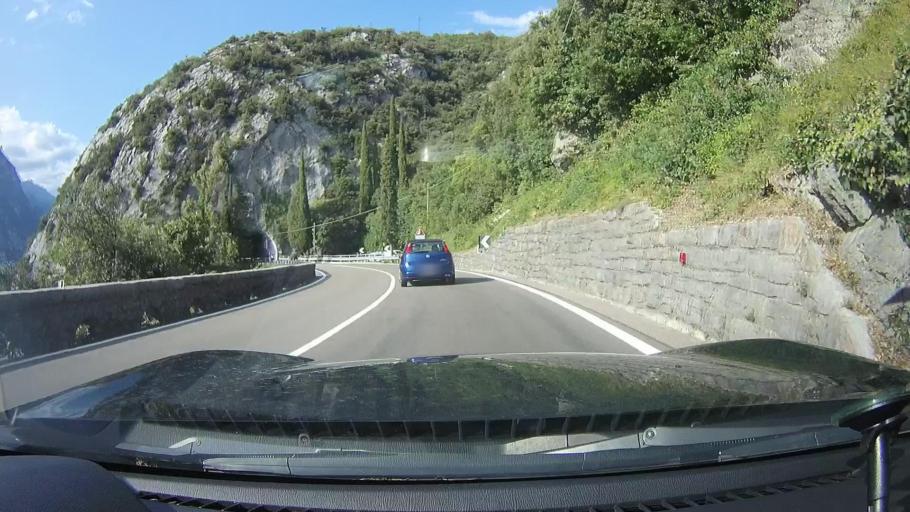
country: IT
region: Trentino-Alto Adige
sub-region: Provincia di Trento
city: Torbole sul Garda
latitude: 45.8443
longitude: 10.8636
